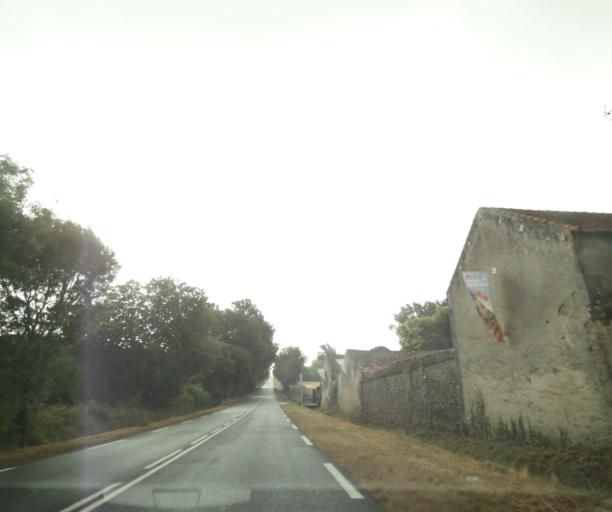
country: FR
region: Pays de la Loire
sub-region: Departement de la Vendee
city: Avrille
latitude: 46.4753
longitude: -1.5097
